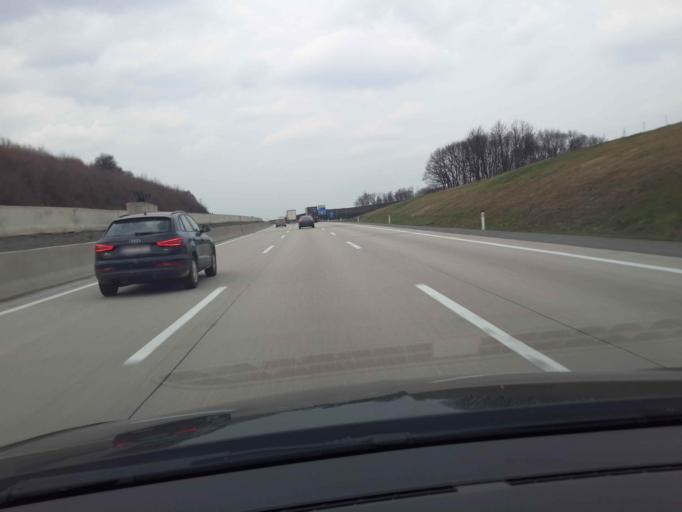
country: AT
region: Lower Austria
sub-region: Politischer Bezirk Sankt Polten
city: Neulengbach
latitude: 48.1716
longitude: 15.8765
